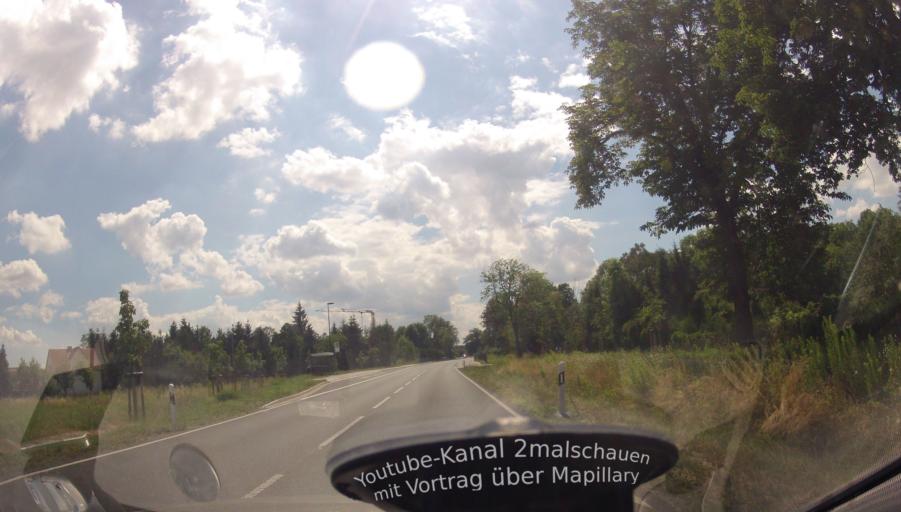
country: DE
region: Saxony
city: Torgau
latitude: 51.5332
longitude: 13.0004
